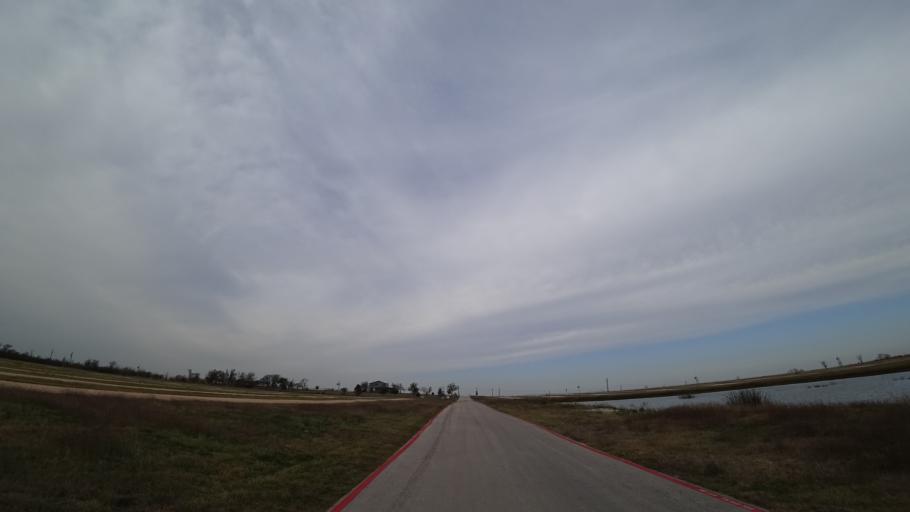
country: US
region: Texas
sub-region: Travis County
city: Garfield
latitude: 30.1370
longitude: -97.6199
